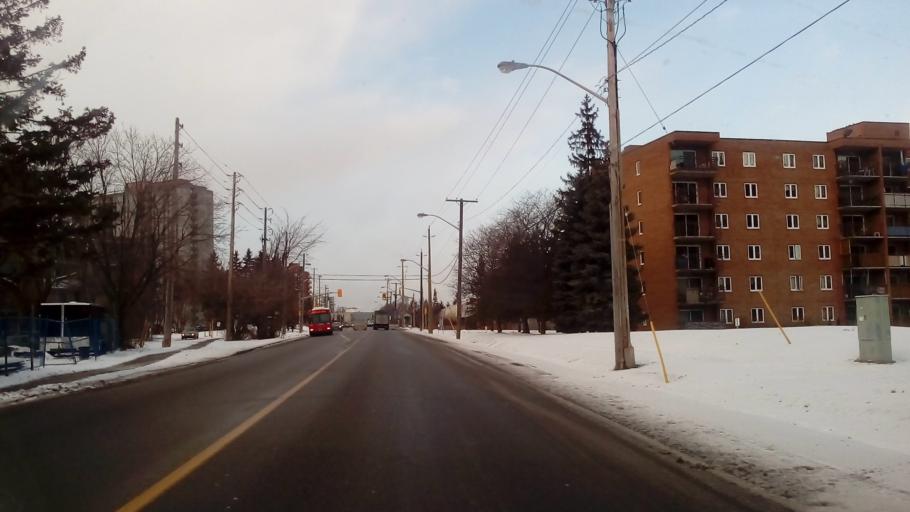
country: CA
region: Ontario
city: Ottawa
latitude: 45.3977
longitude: -75.6172
